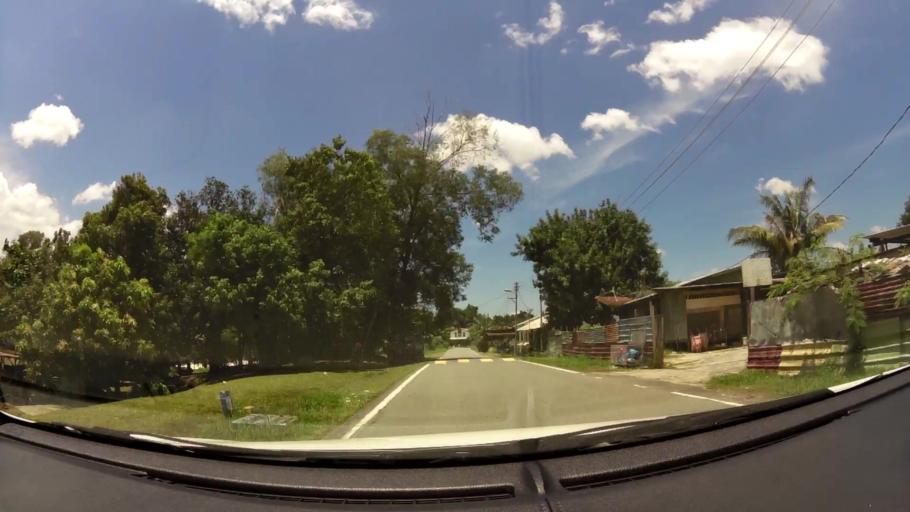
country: BN
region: Brunei and Muara
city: Bandar Seri Begawan
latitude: 4.9425
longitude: 114.9576
